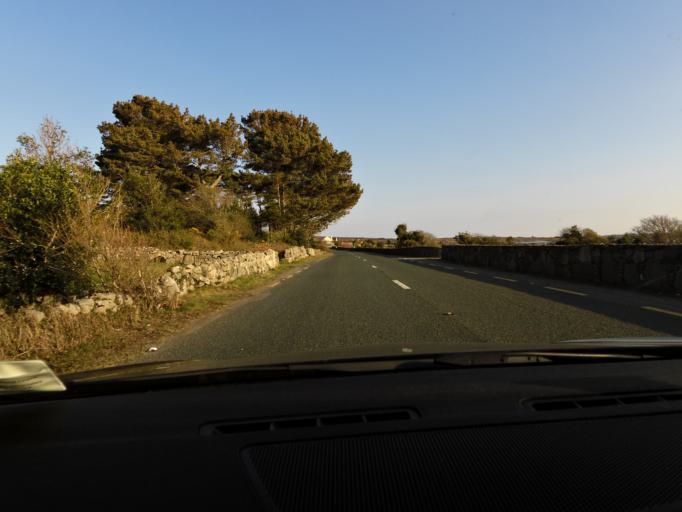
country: IE
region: Connaught
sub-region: County Galway
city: Oughterard
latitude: 53.3844
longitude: -9.6059
